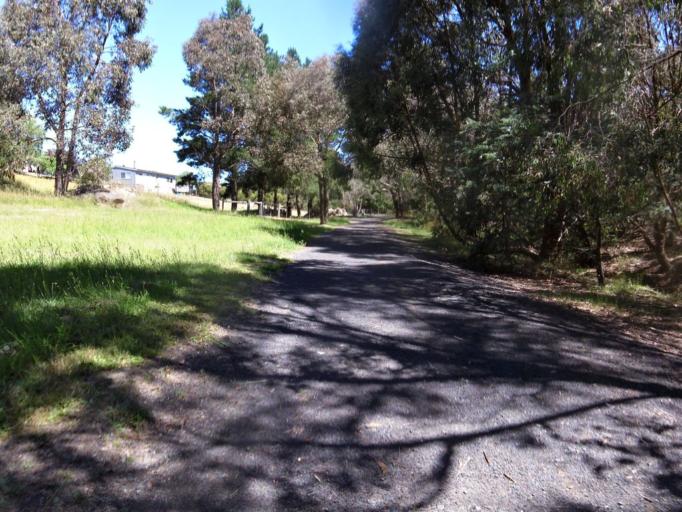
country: AU
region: Victoria
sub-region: Whittlesea
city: Whittlesea
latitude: -37.3642
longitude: 145.0358
